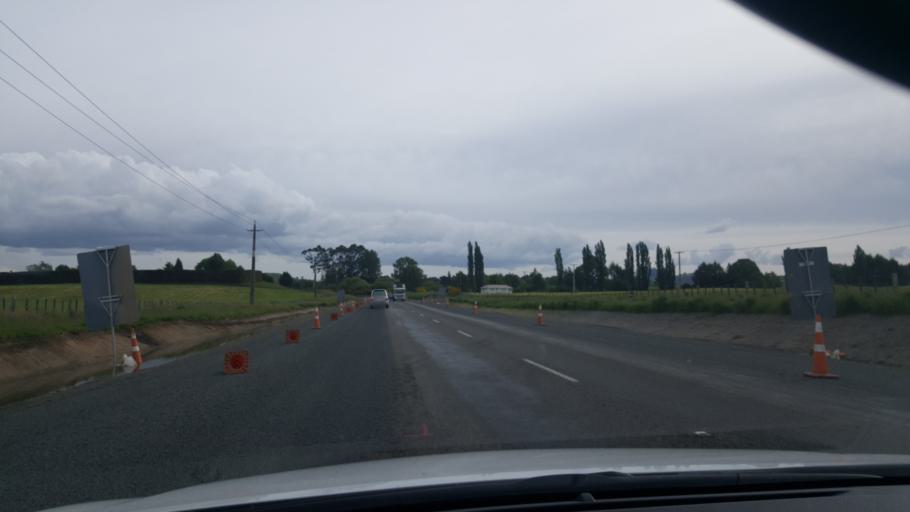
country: NZ
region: Bay of Plenty
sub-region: Rotorua District
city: Rotorua
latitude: -38.4113
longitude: 176.3218
